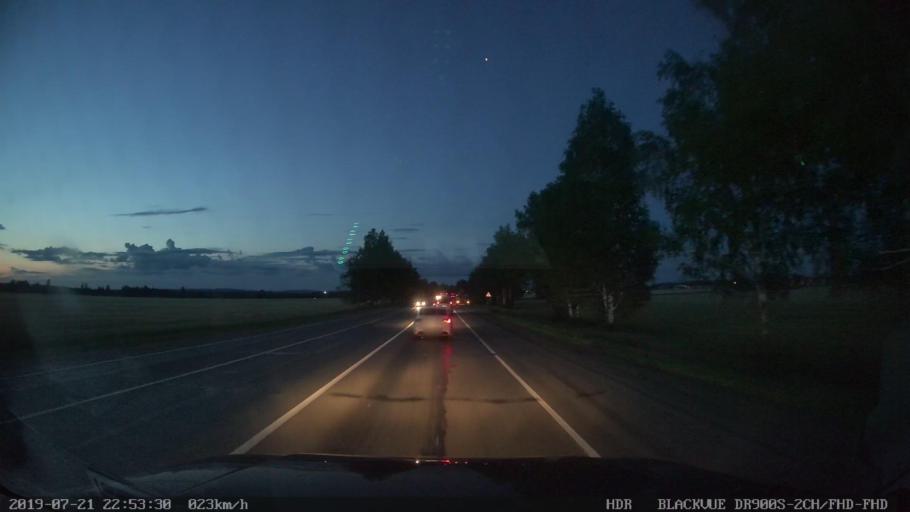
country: RU
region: Perm
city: Ust'-Kachka
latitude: 58.0707
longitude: 55.6324
